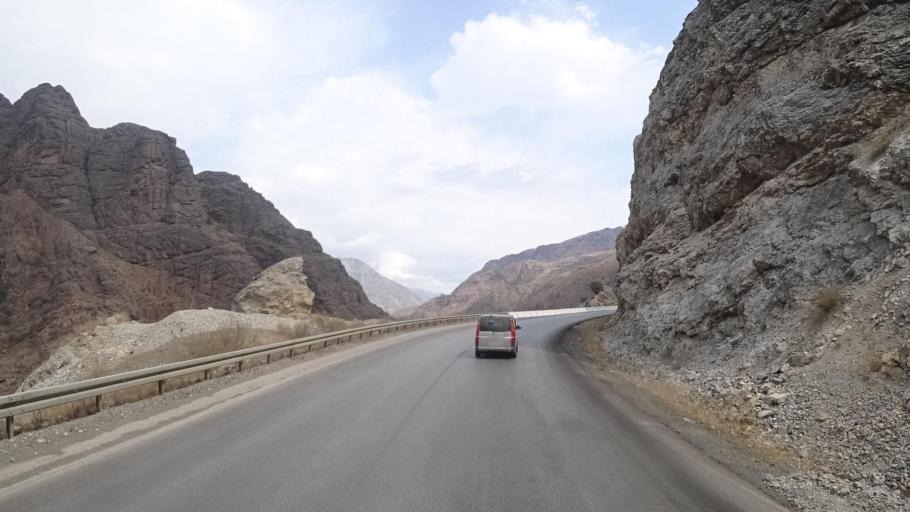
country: KG
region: Jalal-Abad
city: Tash-Kumyr
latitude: 41.5845
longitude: 72.5505
